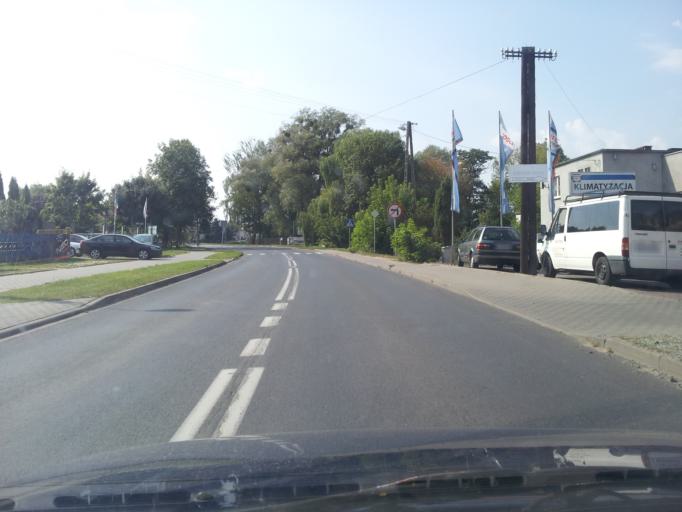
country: PL
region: Kujawsko-Pomorskie
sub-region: Powiat brodnicki
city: Brodnica
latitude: 53.2535
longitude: 19.4205
